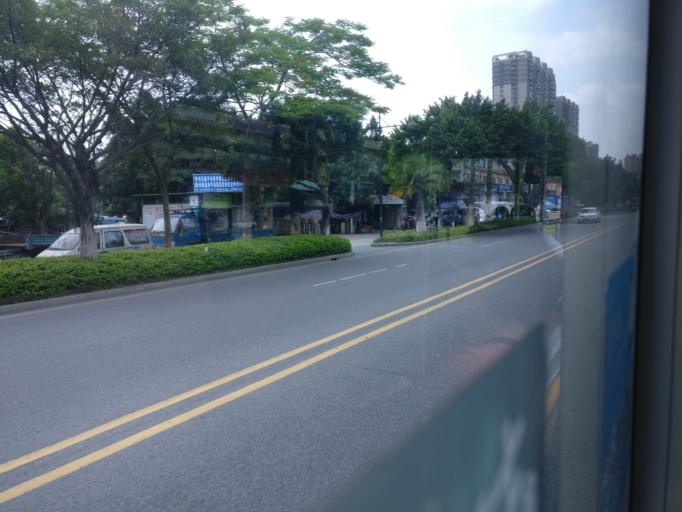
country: CN
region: Guangdong
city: Xiaoguwei
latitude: 23.0367
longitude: 113.3357
